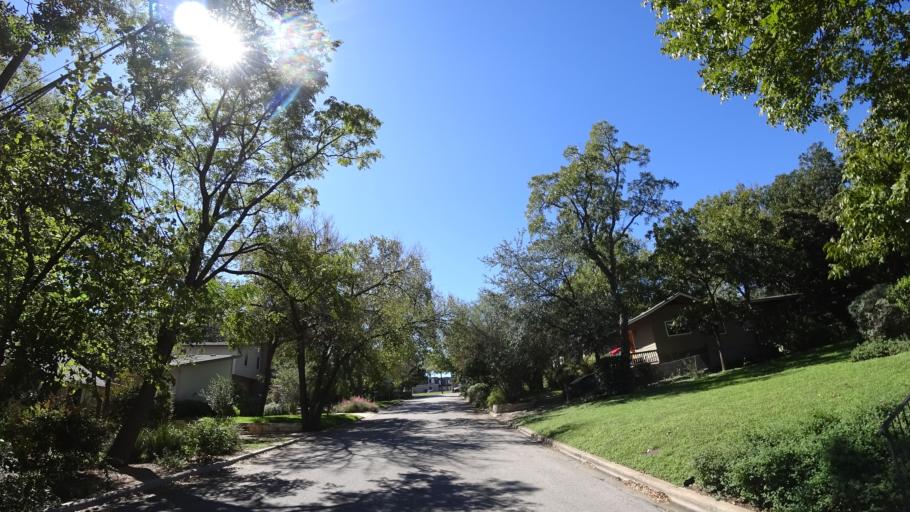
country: US
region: Texas
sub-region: Travis County
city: Austin
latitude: 30.2373
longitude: -97.7431
